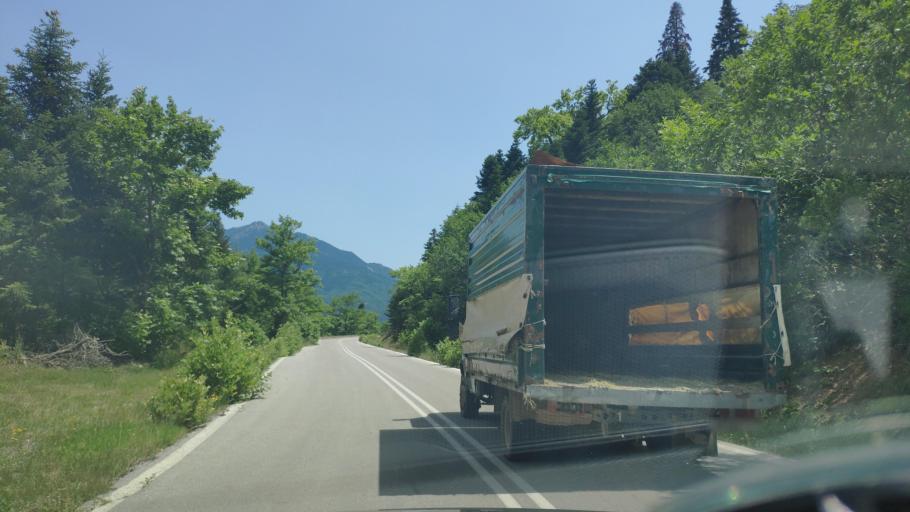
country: GR
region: Thessaly
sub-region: Nomos Kardhitsas
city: Anthiro
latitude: 39.2701
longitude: 21.3490
